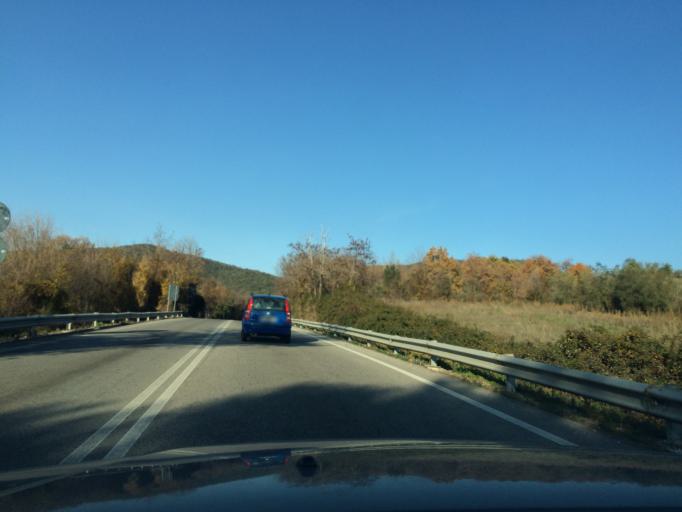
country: IT
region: Umbria
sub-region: Provincia di Terni
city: Fornole
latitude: 42.5333
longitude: 12.4754
